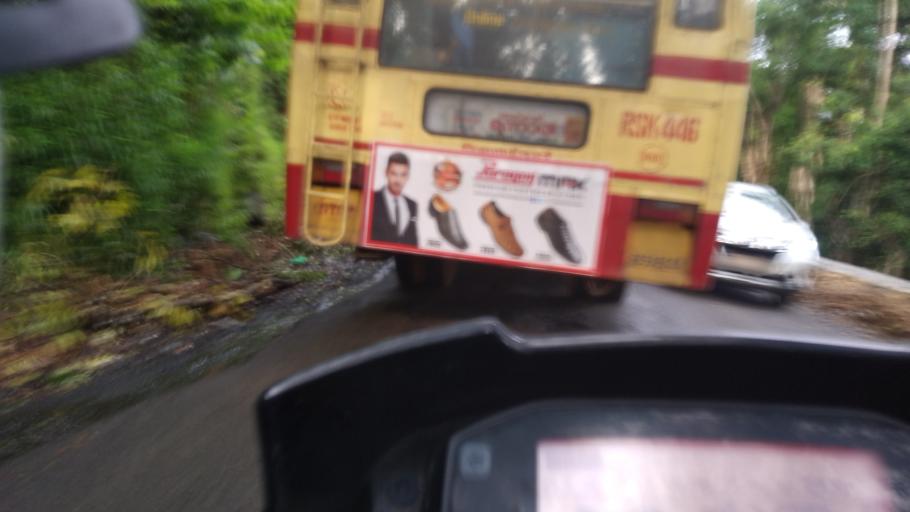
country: IN
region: Kerala
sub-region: Idukki
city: Kuttampuzha
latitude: 10.0656
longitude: 76.7739
